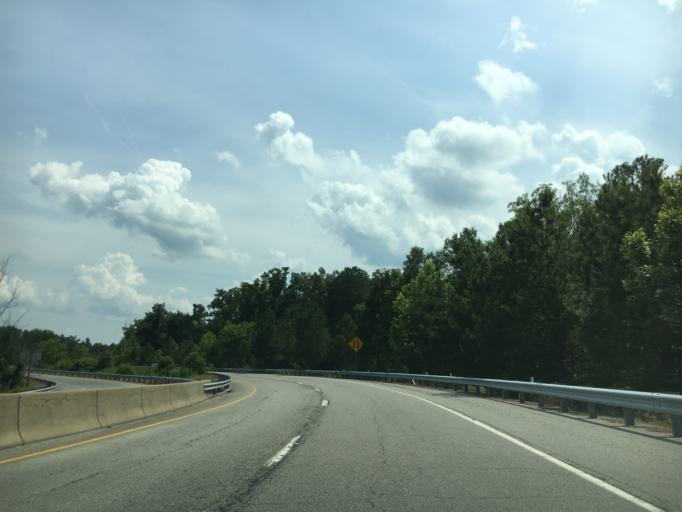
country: US
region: Virginia
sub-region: Henrico County
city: Short Pump
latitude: 37.6637
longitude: -77.6607
